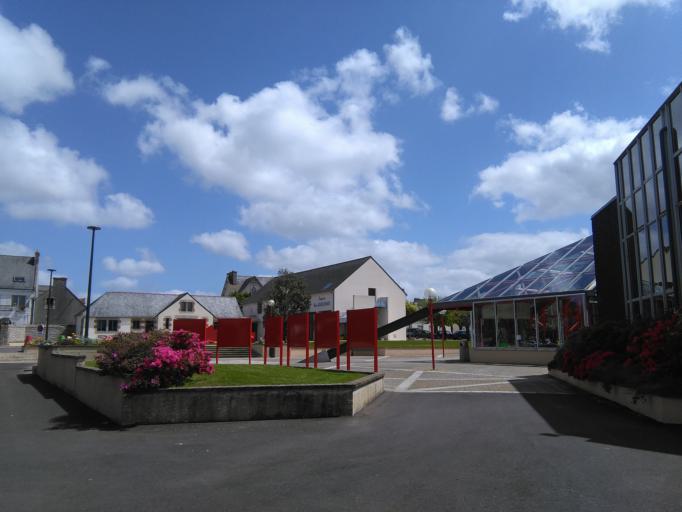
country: FR
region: Brittany
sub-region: Departement du Finistere
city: Landivisiau
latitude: 48.5096
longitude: -4.0687
